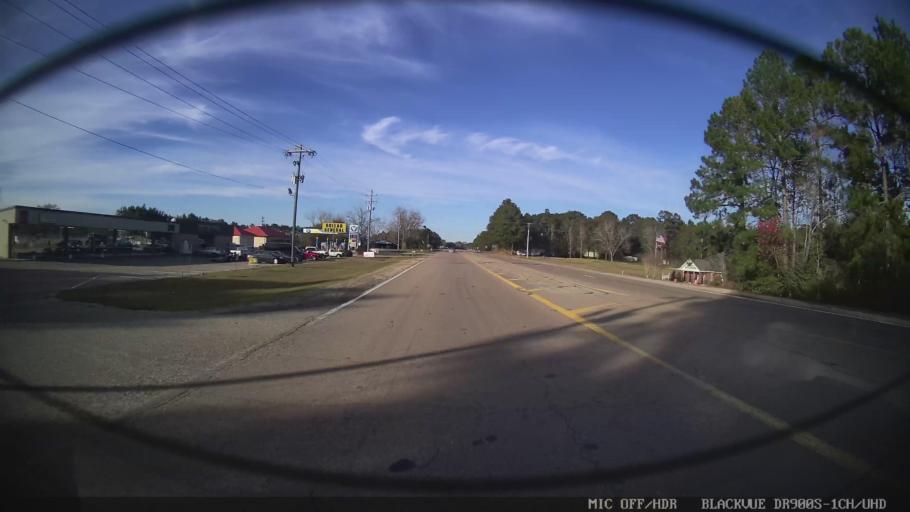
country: US
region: Mississippi
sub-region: Forrest County
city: Hattiesburg
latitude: 31.2359
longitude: -89.3023
